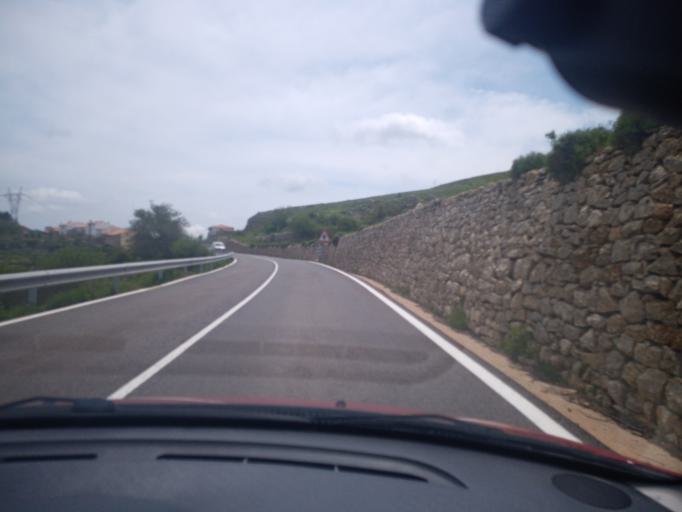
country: ES
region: Valencia
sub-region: Provincia de Castello
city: Ares del Maestre
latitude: 40.4559
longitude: -0.1448
